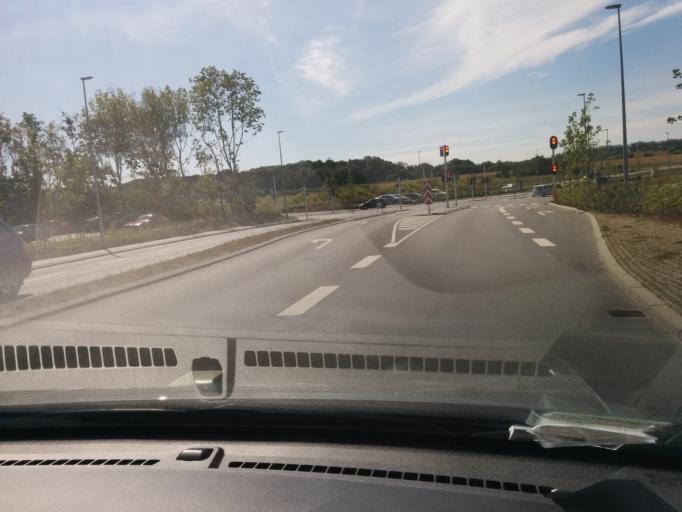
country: DK
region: Central Jutland
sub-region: Arhus Kommune
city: Arhus
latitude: 56.1899
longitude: 10.1765
